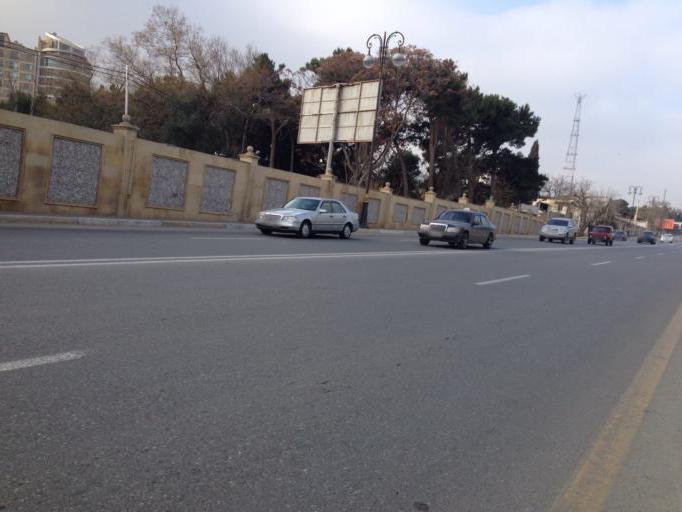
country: AZ
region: Baki
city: Baku
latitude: 40.3935
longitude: 49.8552
